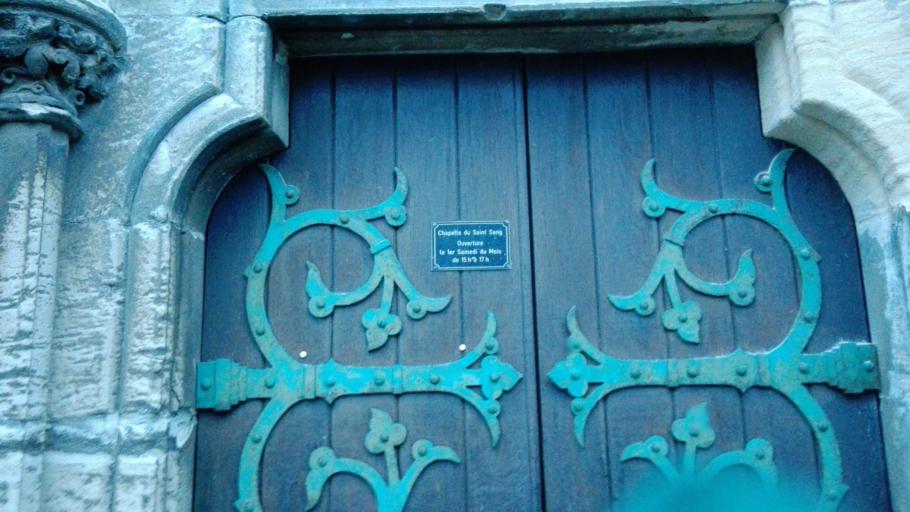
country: FR
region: Nord-Pas-de-Calais
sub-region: Departement du Pas-de-Calais
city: Boulogne-sur-Mer
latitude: 50.7130
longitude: 1.6142
